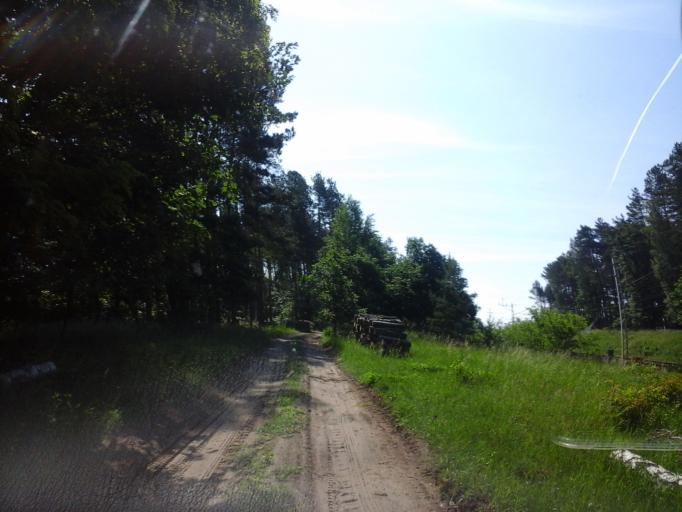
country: PL
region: West Pomeranian Voivodeship
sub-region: Powiat choszczenski
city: Bierzwnik
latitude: 53.0125
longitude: 15.6836
